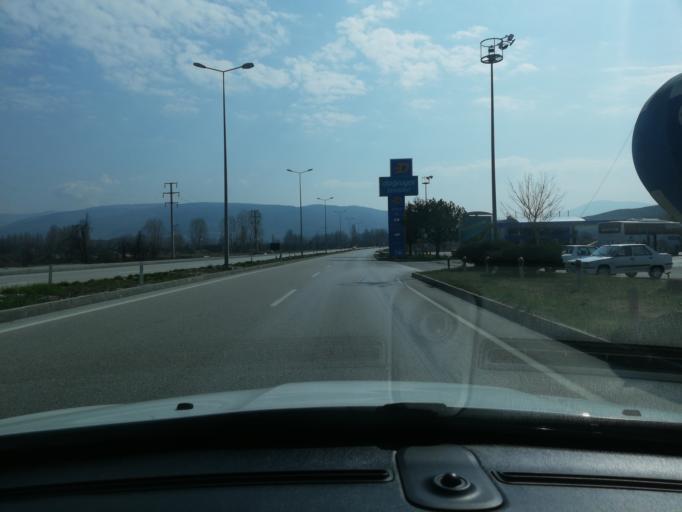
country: TR
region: Cankiri
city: Ilgaz
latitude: 40.9085
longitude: 33.6313
